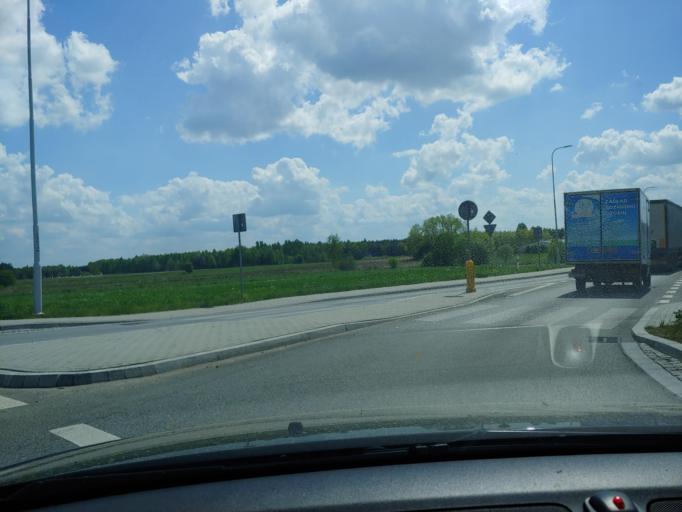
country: PL
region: Subcarpathian Voivodeship
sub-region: Powiat mielecki
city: Radomysl Wielki
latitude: 50.1866
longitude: 21.2636
